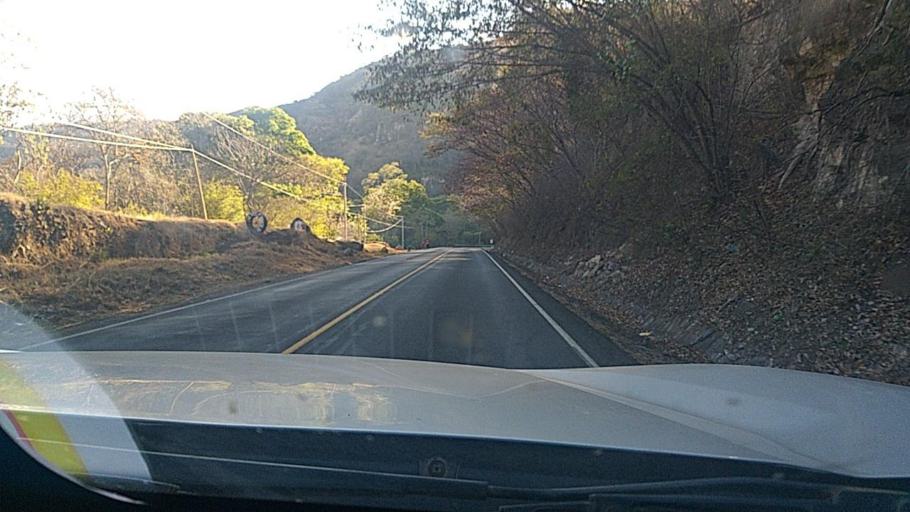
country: NI
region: Esteli
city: Condega
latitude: 13.2736
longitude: -86.3535
